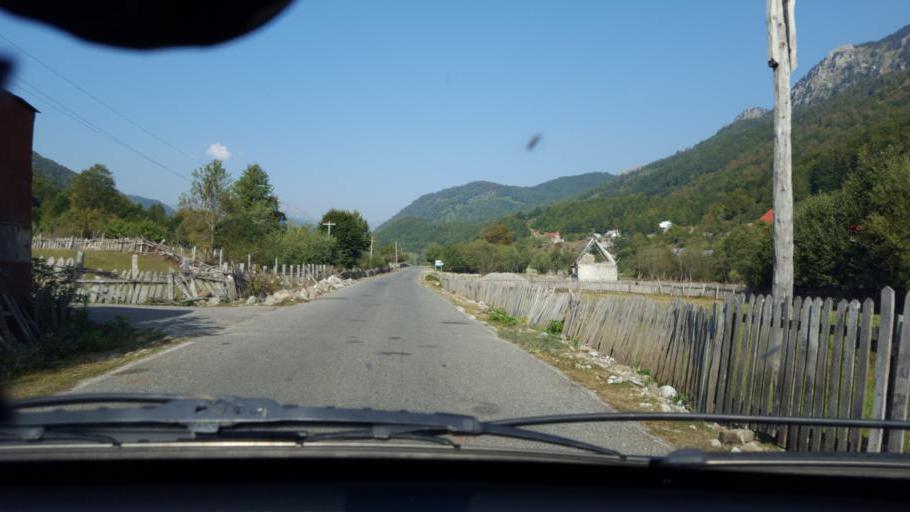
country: ME
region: Andrijevica
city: Andrijevica
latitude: 42.5857
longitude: 19.7233
